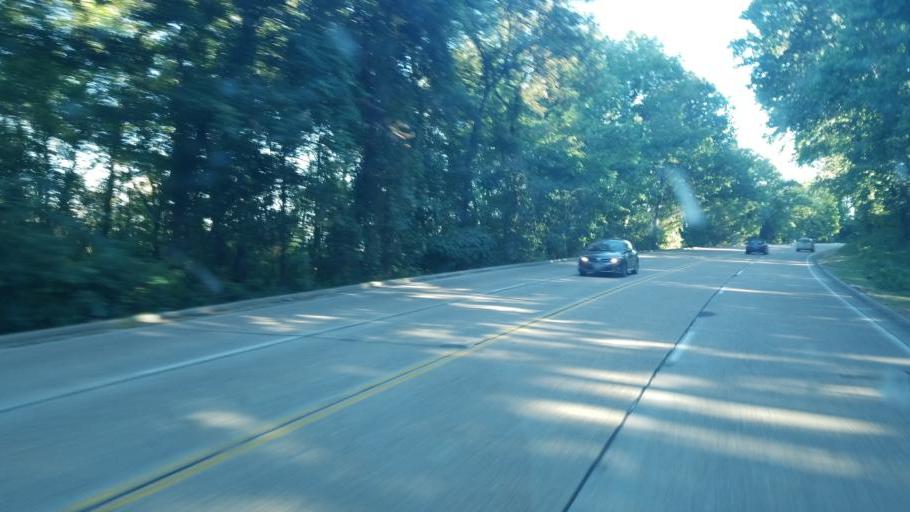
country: US
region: Virginia
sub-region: Fairfax County
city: Belle Haven
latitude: 38.7619
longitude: -77.0504
